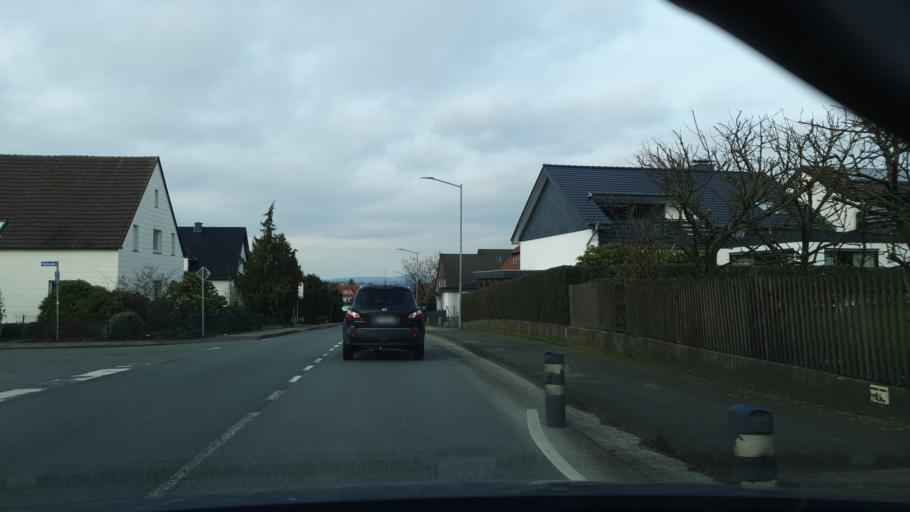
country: DE
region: North Rhine-Westphalia
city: Spenge
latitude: 52.1280
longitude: 8.4884
